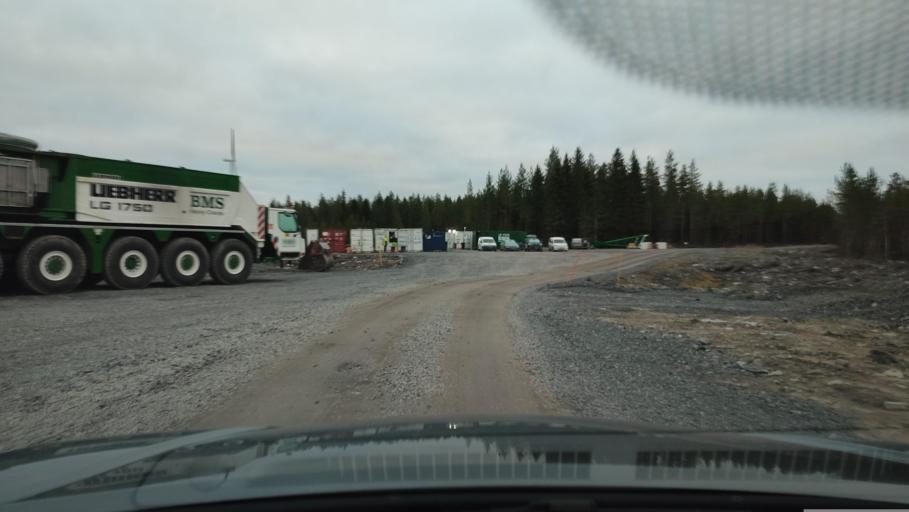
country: FI
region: Southern Ostrobothnia
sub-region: Suupohja
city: Karijoki
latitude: 62.1881
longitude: 21.5636
